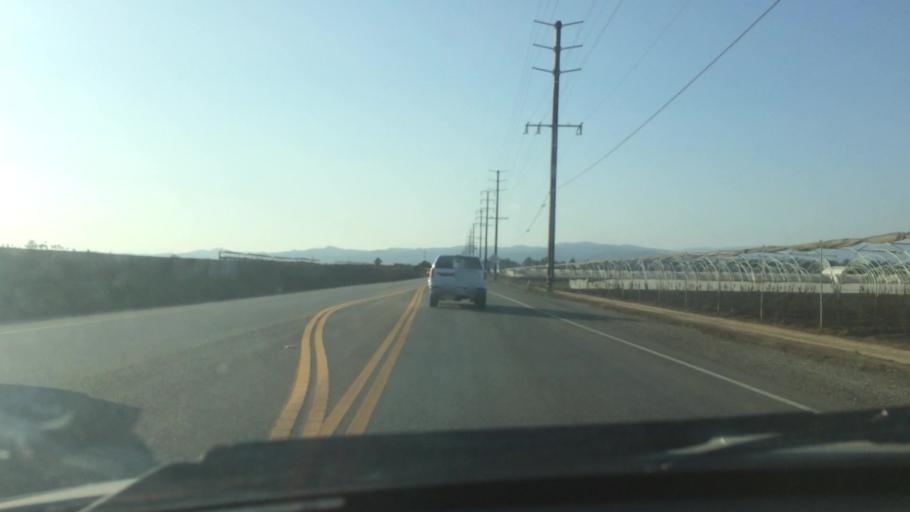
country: US
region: California
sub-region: Ventura County
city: Saticoy
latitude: 34.2601
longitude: -119.1151
